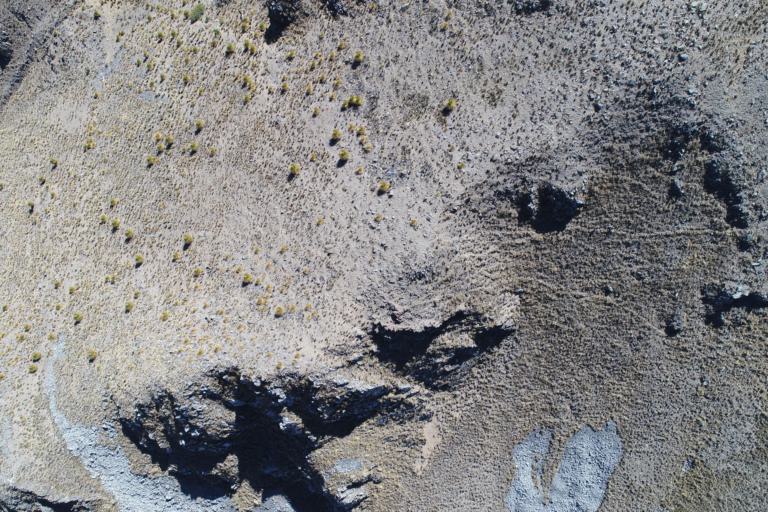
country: BO
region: La Paz
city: Viloco
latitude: -16.8072
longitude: -67.5463
